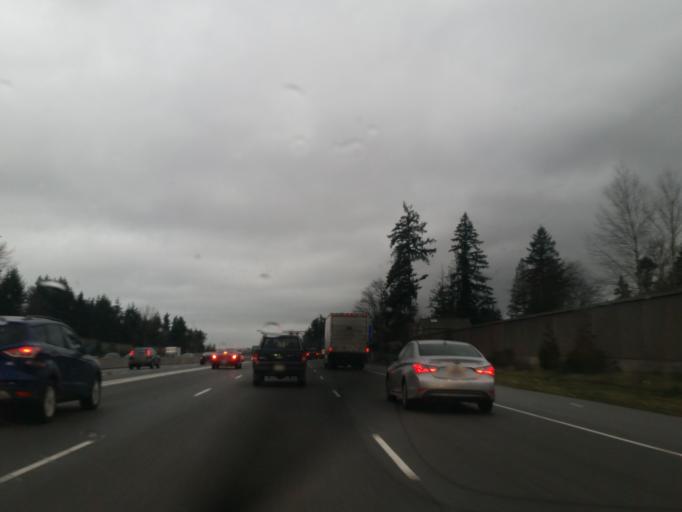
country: US
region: Washington
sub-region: King County
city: Kirkland
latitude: 47.6859
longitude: -122.1825
